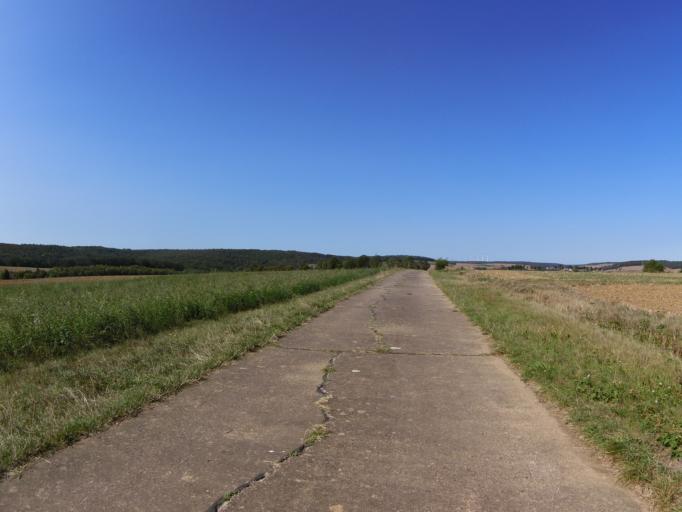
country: DE
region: Bavaria
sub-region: Regierungsbezirk Unterfranken
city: Waldbrunn
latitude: 49.7618
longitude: 9.7906
